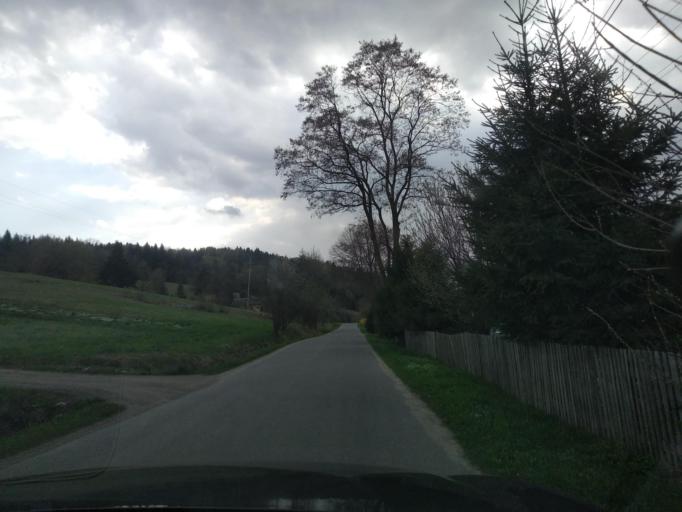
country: PL
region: Subcarpathian Voivodeship
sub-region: Powiat leski
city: Baligrod
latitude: 49.3506
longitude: 22.2606
